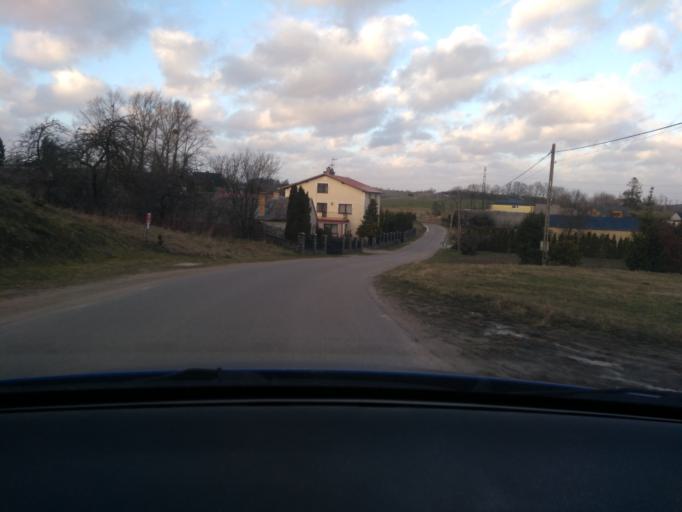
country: PL
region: Pomeranian Voivodeship
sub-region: Powiat kartuski
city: Przodkowo
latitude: 54.4179
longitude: 18.2808
